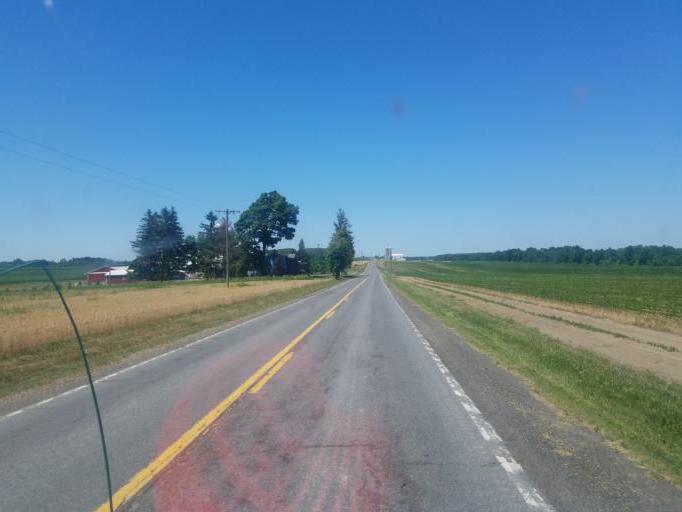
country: US
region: New York
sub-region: Yates County
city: Penn Yan
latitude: 42.7261
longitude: -76.9983
